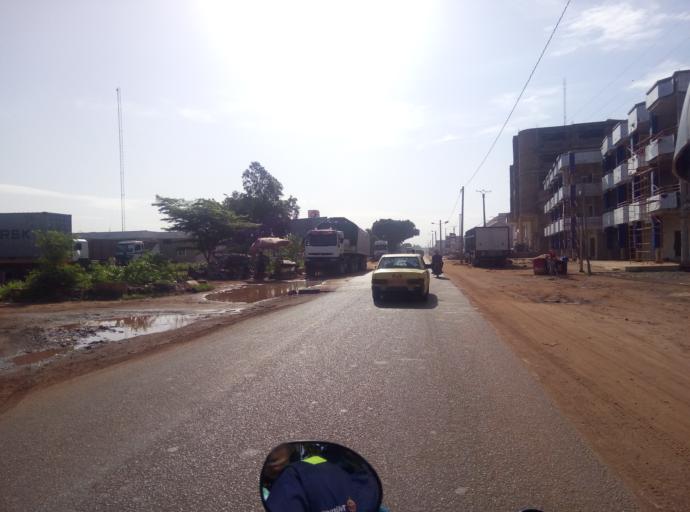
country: ML
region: Bamako
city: Bamako
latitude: 12.6525
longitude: -7.9438
